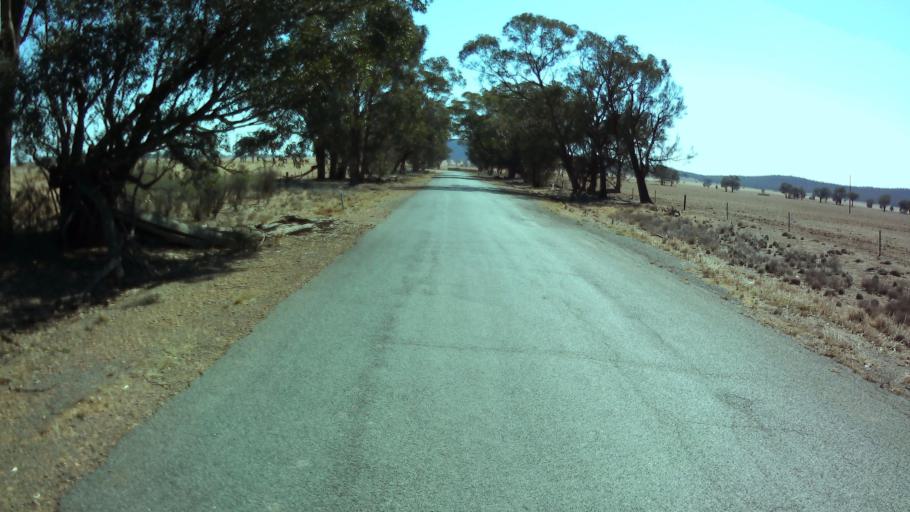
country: AU
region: New South Wales
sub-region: Weddin
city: Grenfell
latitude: -33.7075
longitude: 147.9155
